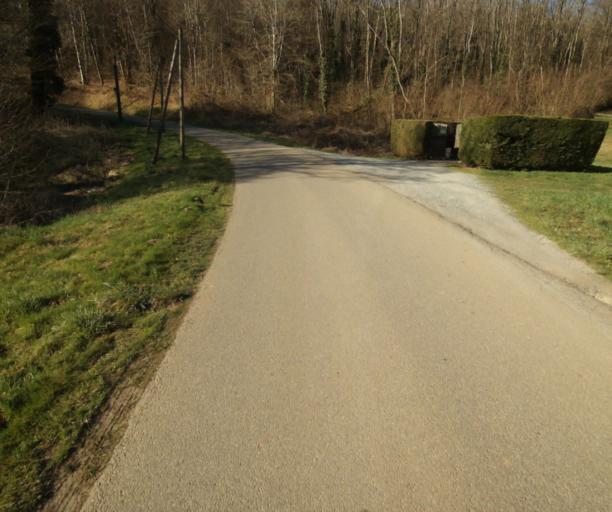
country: FR
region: Limousin
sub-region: Departement de la Correze
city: Seilhac
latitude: 45.3918
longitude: 1.7582
